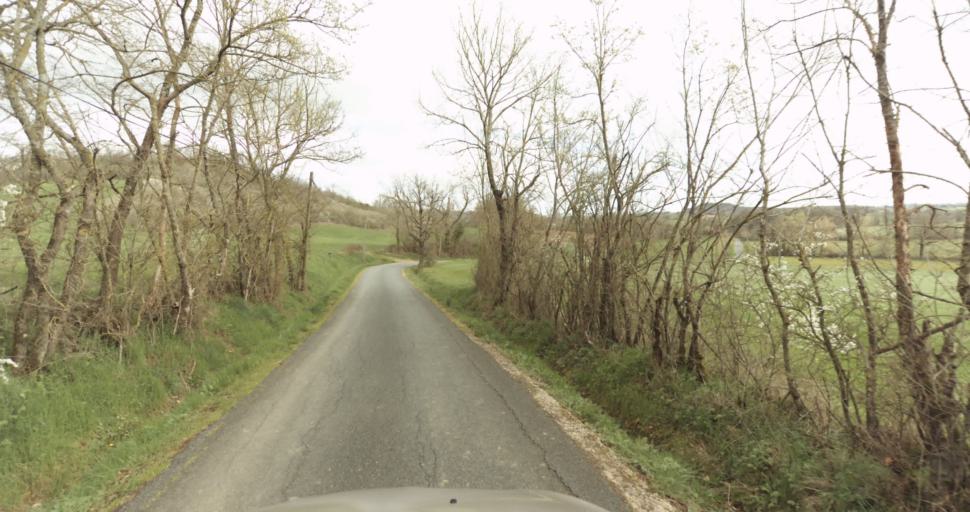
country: FR
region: Midi-Pyrenees
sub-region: Departement du Tarn
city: Puygouzon
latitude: 43.8760
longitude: 2.1943
